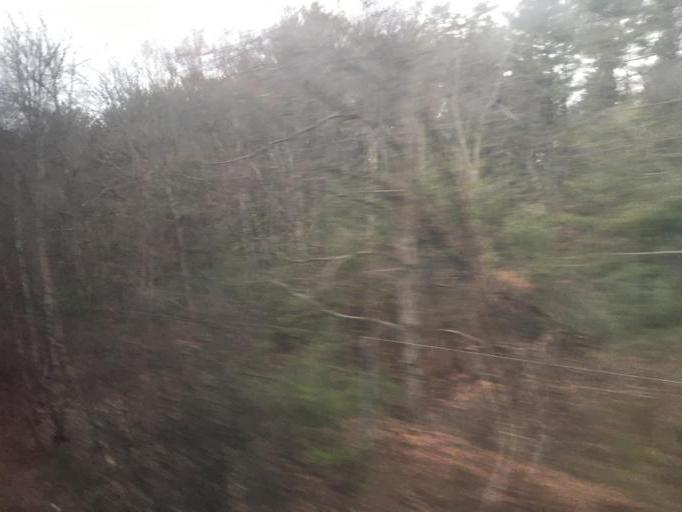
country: US
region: Massachusetts
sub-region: Norfolk County
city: Sharon
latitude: 42.1308
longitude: -71.1790
